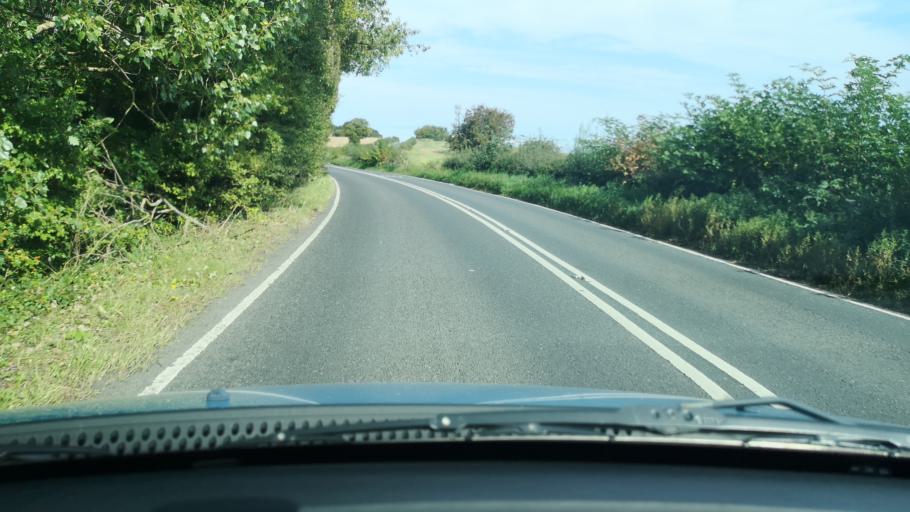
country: GB
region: England
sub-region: City and Borough of Wakefield
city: Walton
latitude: 53.6410
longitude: -1.4802
